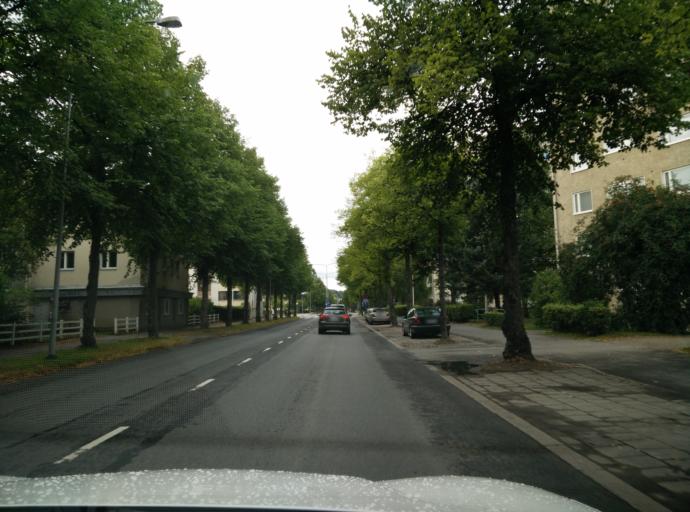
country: FI
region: Haeme
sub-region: Haemeenlinna
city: Haemeenlinna
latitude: 60.9964
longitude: 24.4436
